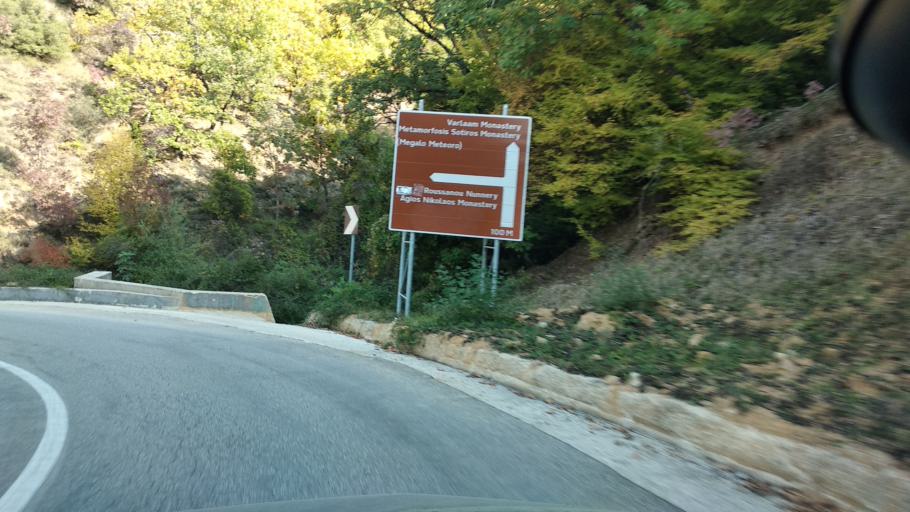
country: GR
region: Thessaly
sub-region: Trikala
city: Kastraki
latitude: 39.7246
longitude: 21.6376
